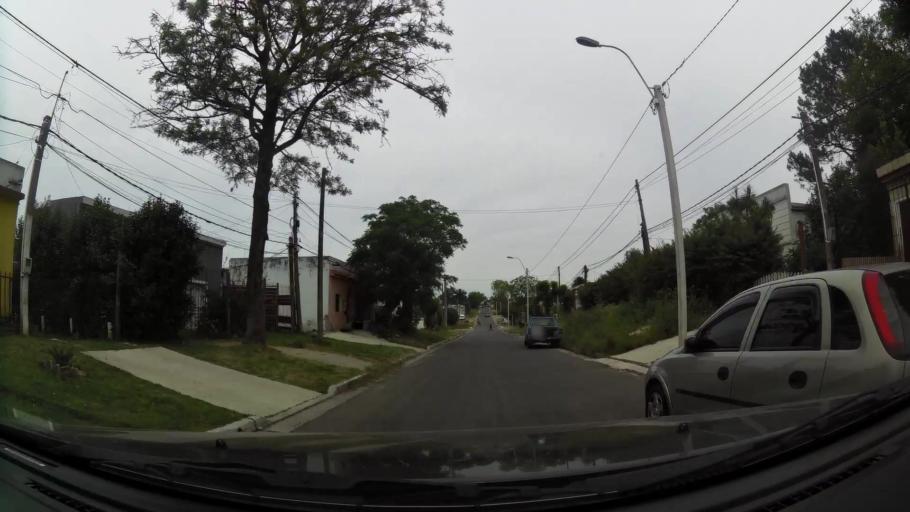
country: UY
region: Canelones
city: Las Piedras
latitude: -34.7299
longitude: -56.2108
